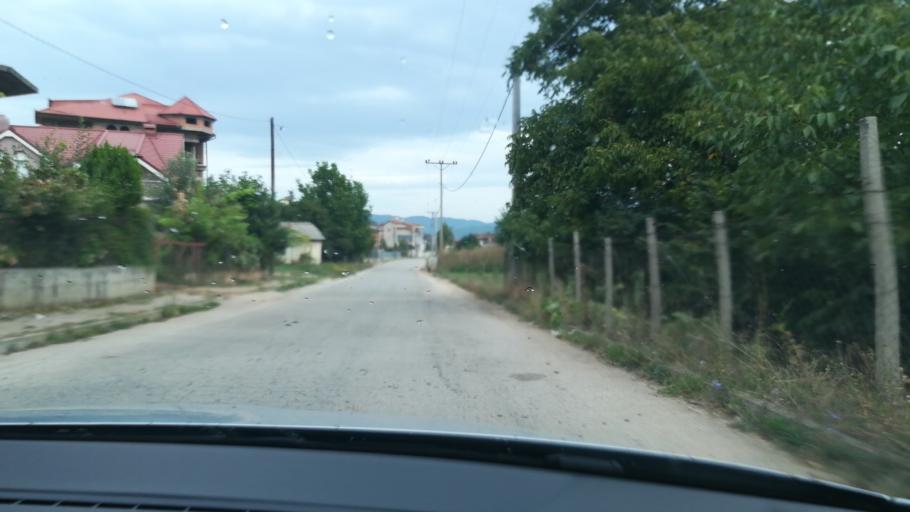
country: MK
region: Kicevo
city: Kicevo
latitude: 41.5167
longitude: 20.9504
